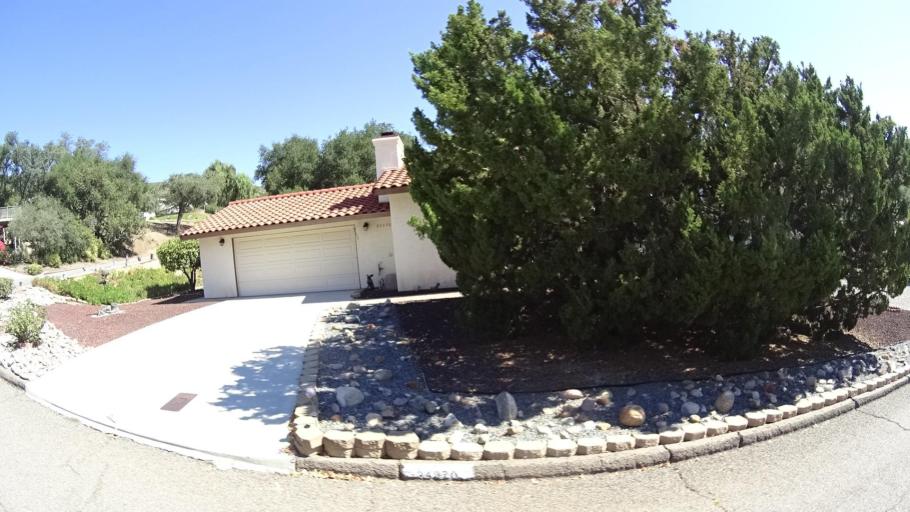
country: US
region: California
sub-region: San Diego County
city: San Diego Country Estates
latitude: 33.0239
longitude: -116.8033
